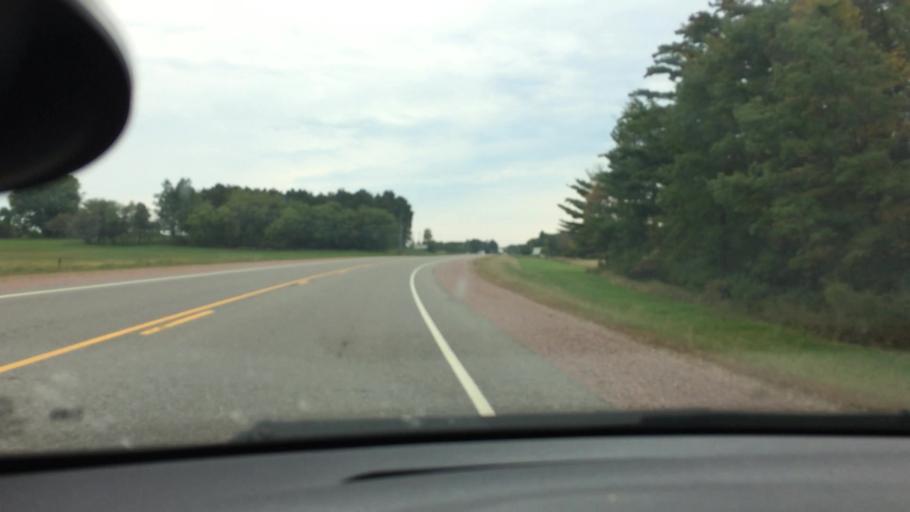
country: US
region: Wisconsin
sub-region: Clark County
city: Neillsville
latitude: 44.5627
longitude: -90.6851
